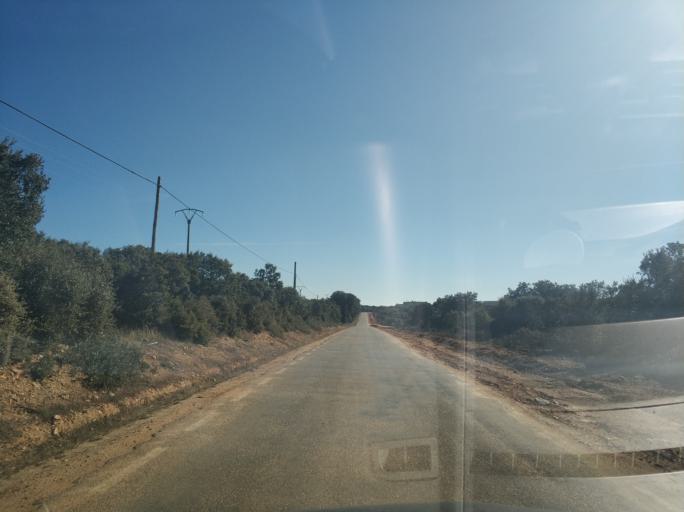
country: ES
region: Castille and Leon
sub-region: Provincia de Salamanca
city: Doninos de Salamanca
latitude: 40.9314
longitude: -5.7438
